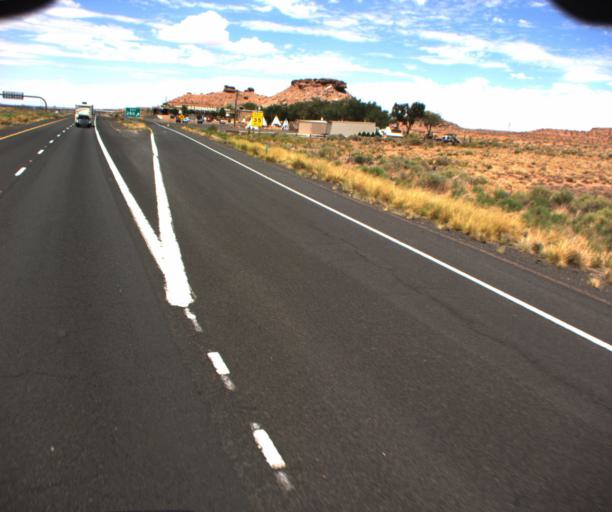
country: US
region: Arizona
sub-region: Navajo County
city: Joseph City
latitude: 34.9182
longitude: -110.2535
